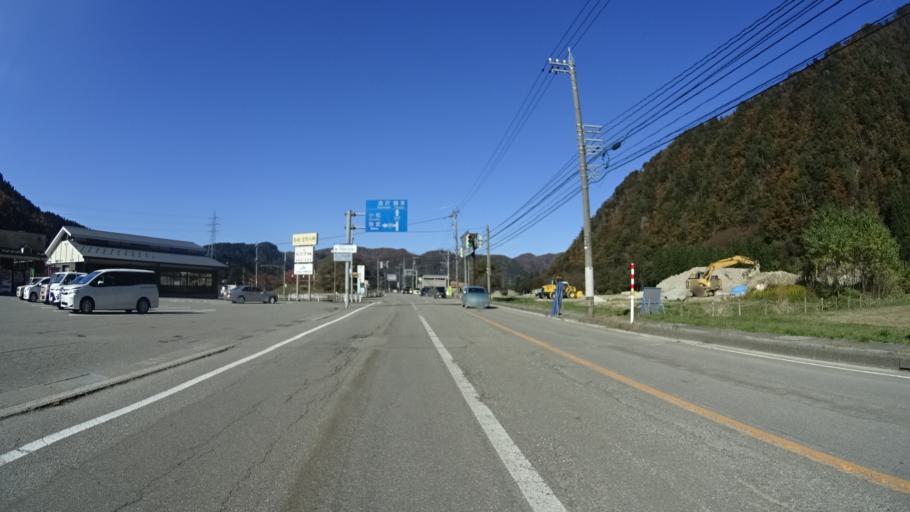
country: JP
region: Ishikawa
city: Tsurugi-asahimachi
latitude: 36.3626
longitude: 136.6175
